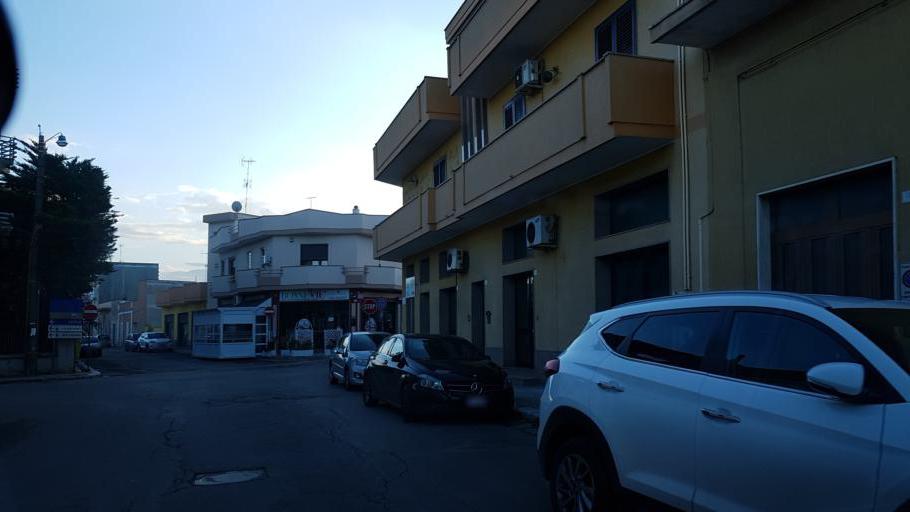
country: IT
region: Apulia
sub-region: Provincia di Lecce
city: Surbo
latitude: 40.3933
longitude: 18.1297
